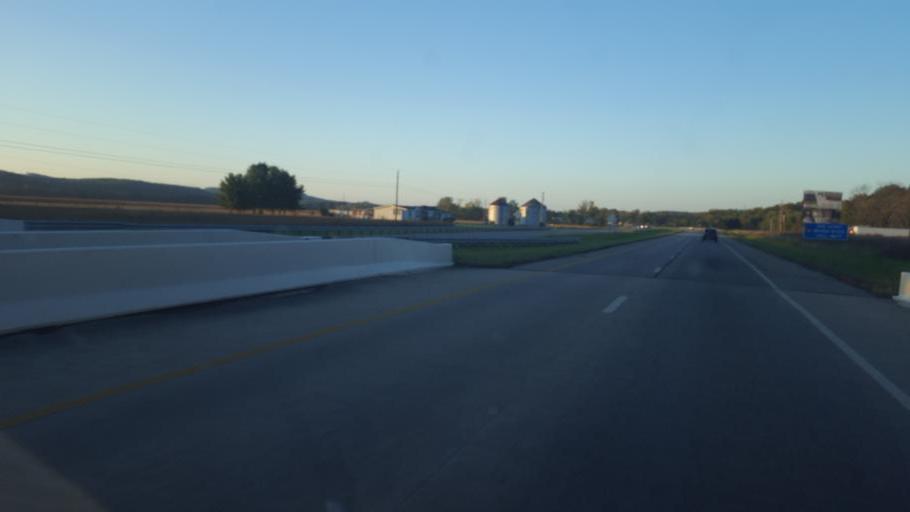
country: US
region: Ohio
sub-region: Scioto County
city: Lucasville
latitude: 38.9701
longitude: -83.0227
